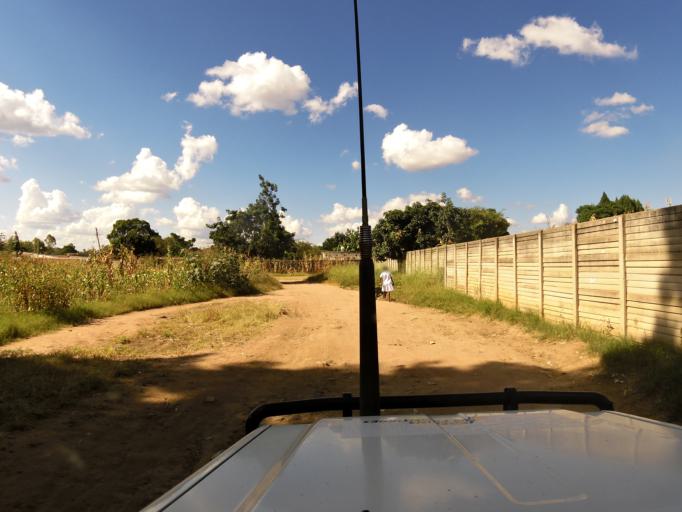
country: ZW
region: Harare
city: Epworth
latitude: -17.8783
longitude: 31.1259
